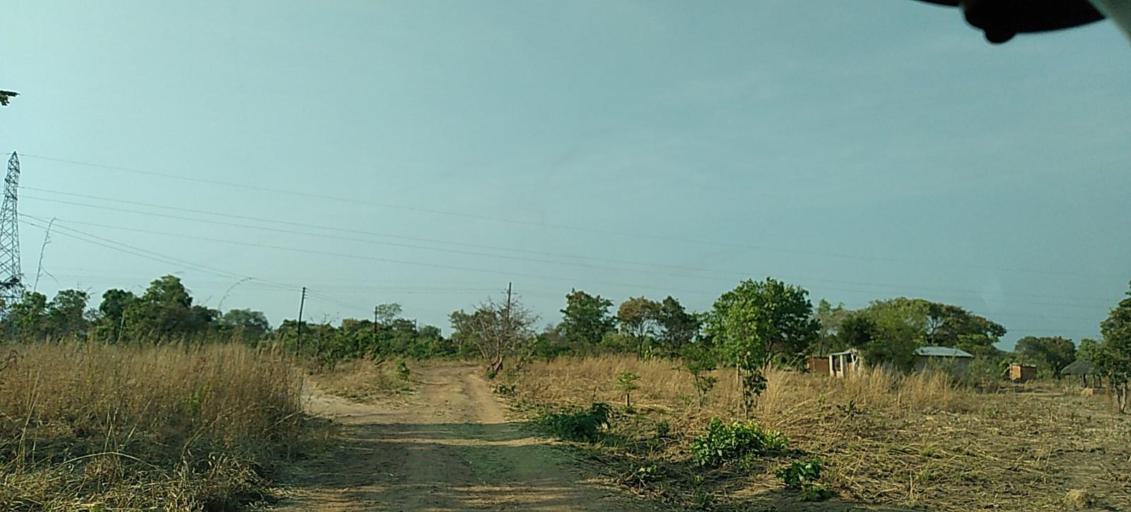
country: ZM
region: North-Western
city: Kalengwa
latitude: -13.1516
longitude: 25.0342
